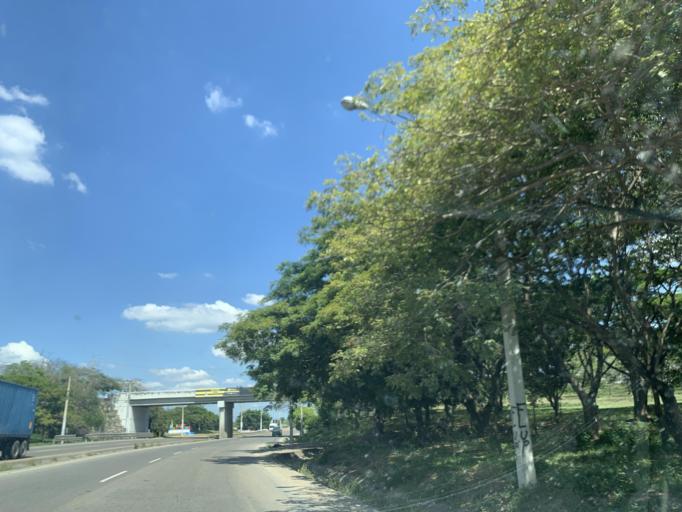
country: DO
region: Santiago
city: Villa Gonzalez
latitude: 19.5343
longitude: -70.7830
